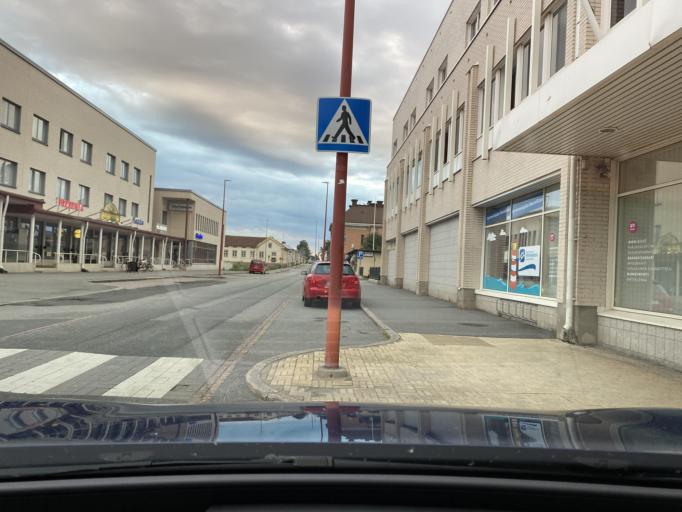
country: FI
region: Northern Ostrobothnia
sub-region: Raahe
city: Raahe
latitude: 64.6850
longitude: 24.4791
